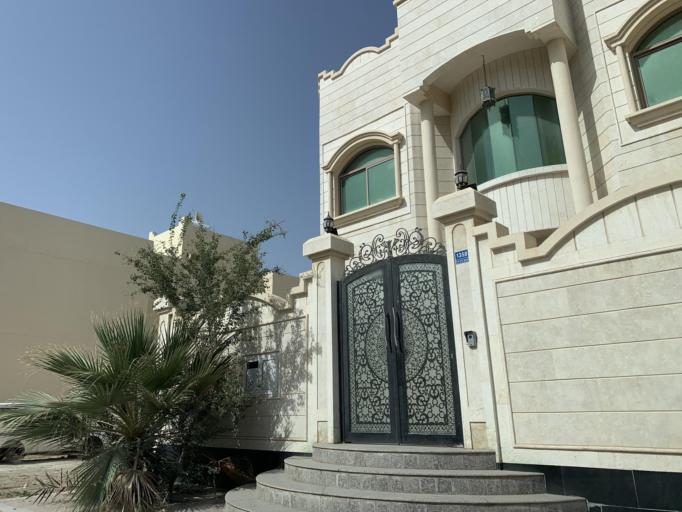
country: BH
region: Northern
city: Sitrah
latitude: 26.1463
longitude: 50.6063
